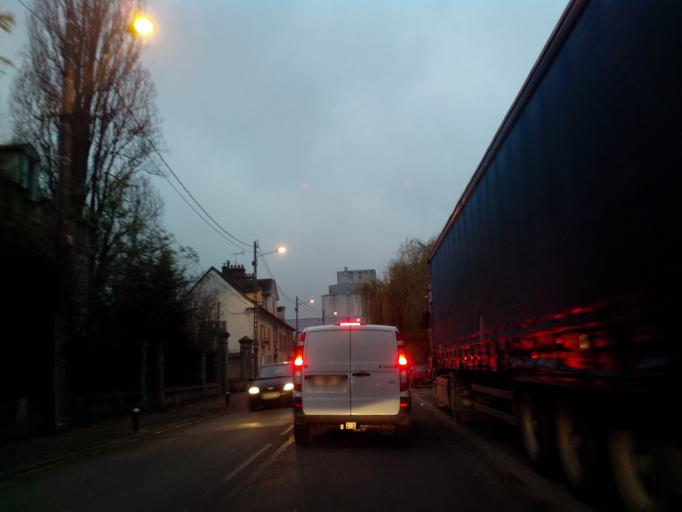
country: FR
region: Ile-de-France
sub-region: Departement de l'Essonne
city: Saint-Germain-les-Corbeil
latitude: 48.6161
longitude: 2.4788
